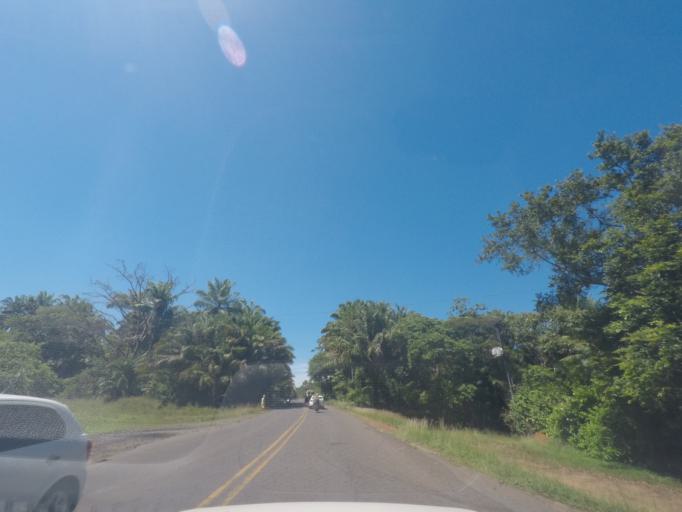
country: BR
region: Bahia
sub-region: Taperoa
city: Taperoa
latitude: -13.4662
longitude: -39.0878
